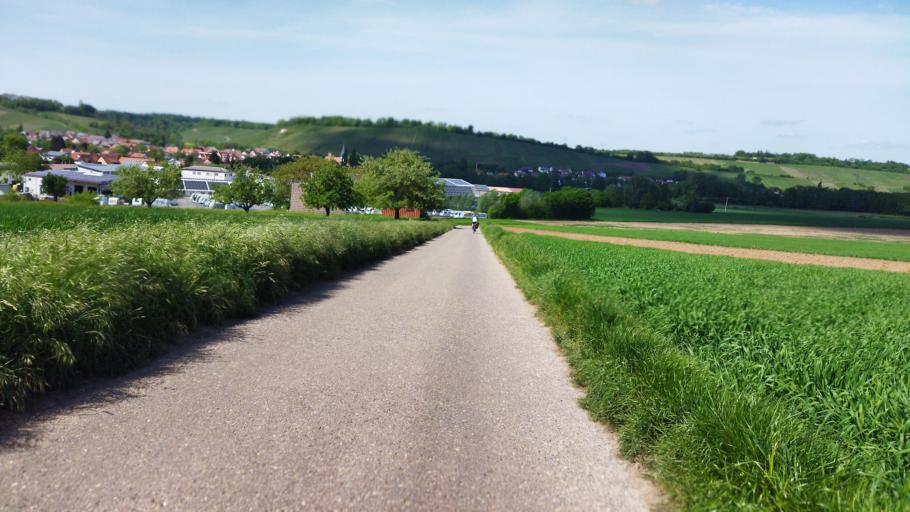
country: DE
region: Baden-Wuerttemberg
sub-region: Regierungsbezirk Stuttgart
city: Pfaffenhofen
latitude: 49.0568
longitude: 8.9801
